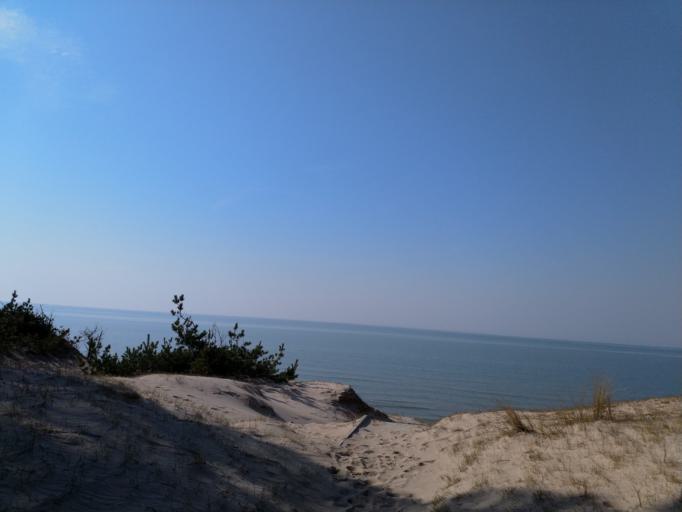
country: LV
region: Alsunga
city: Alsunga
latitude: 57.1596
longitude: 21.4082
